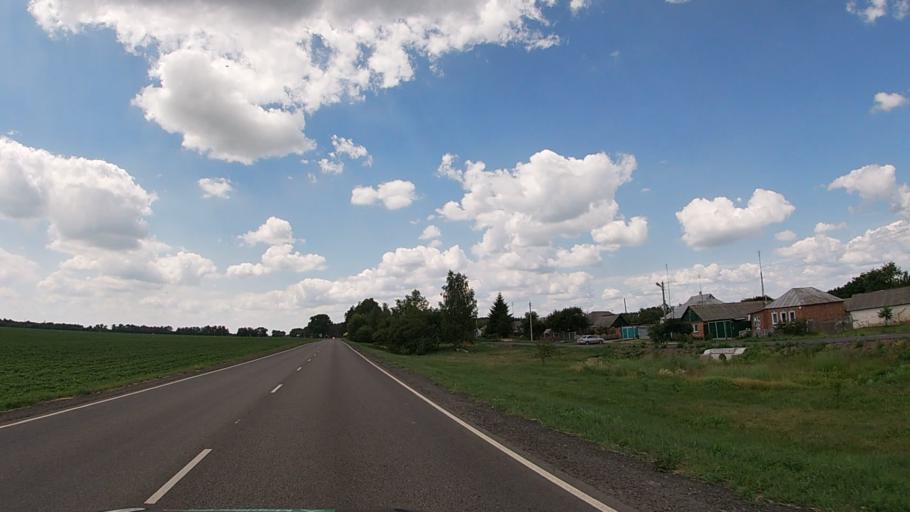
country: RU
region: Belgorod
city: Golovchino
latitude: 50.5100
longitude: 35.7547
